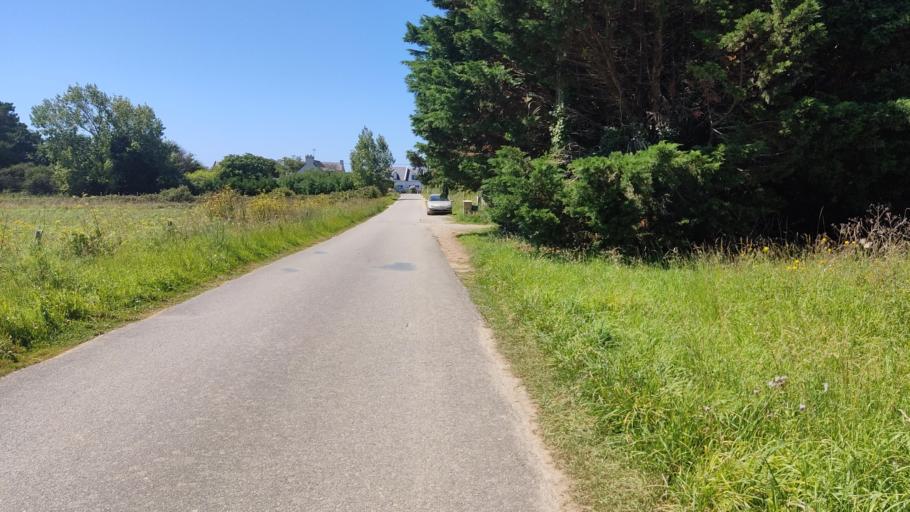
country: FR
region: Brittany
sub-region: Departement du Morbihan
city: Groix
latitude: 47.6335
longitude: -3.4215
